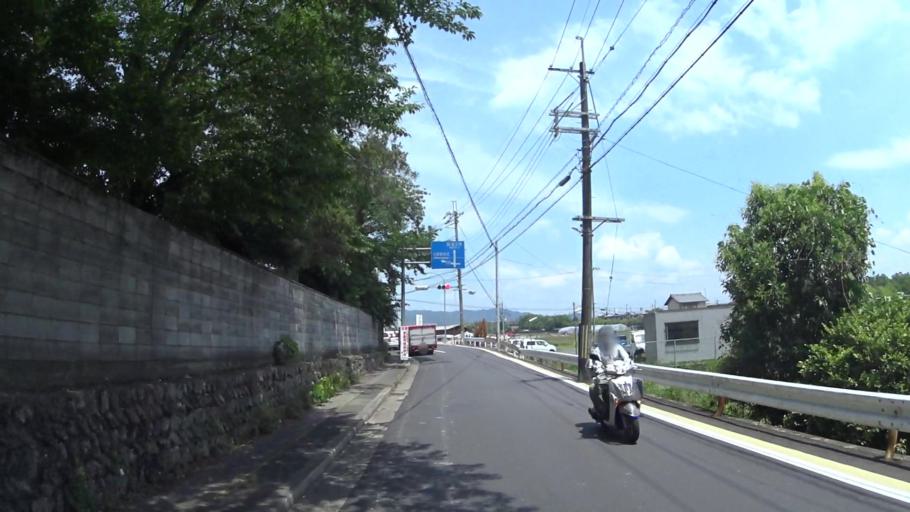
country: JP
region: Kyoto
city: Muko
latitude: 34.9537
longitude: 135.6678
